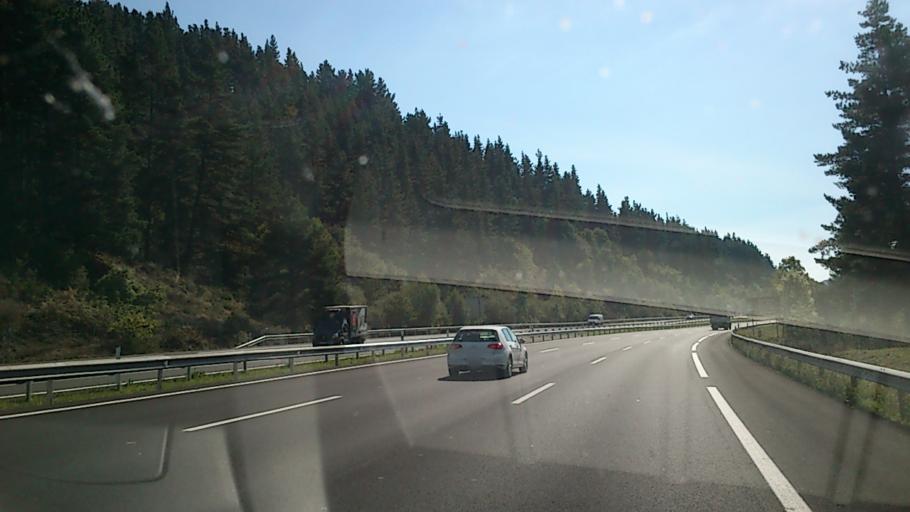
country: ES
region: Basque Country
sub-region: Provincia de Alava
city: Lezama
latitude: 43.0297
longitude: -2.9121
